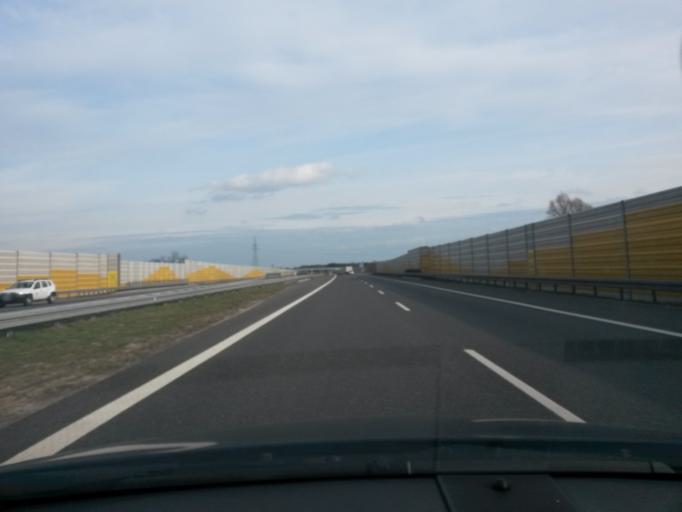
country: PL
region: Lodz Voivodeship
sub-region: Powiat leczycki
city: Swinice Warckie
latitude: 52.0426
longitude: 18.8603
